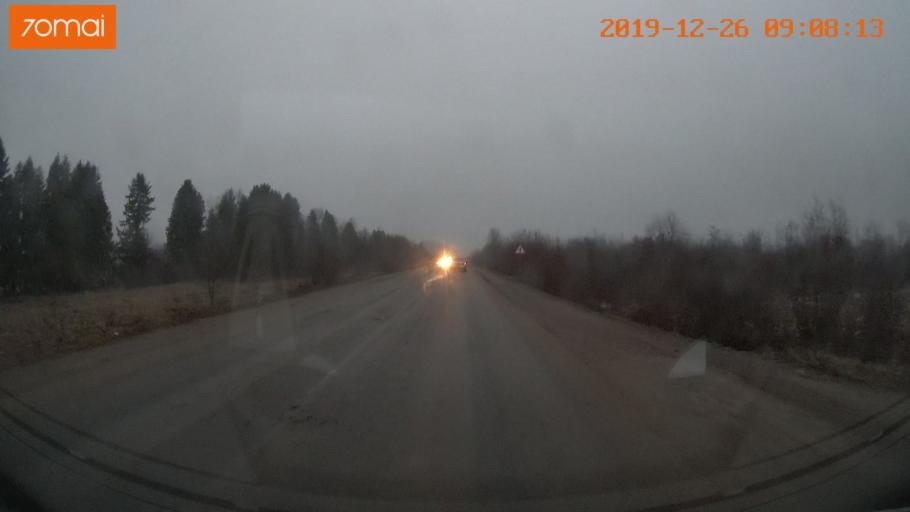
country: RU
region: Vologda
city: Gryazovets
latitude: 58.8545
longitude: 40.2477
